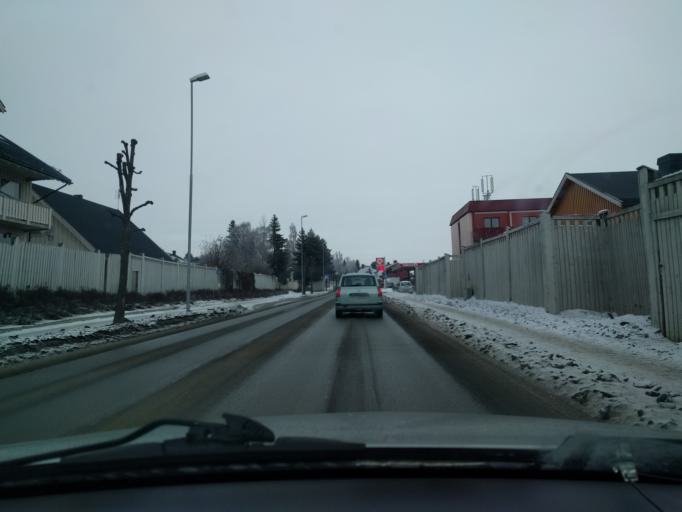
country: NO
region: Hedmark
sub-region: Hamar
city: Hamar
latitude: 60.8009
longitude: 11.0745
